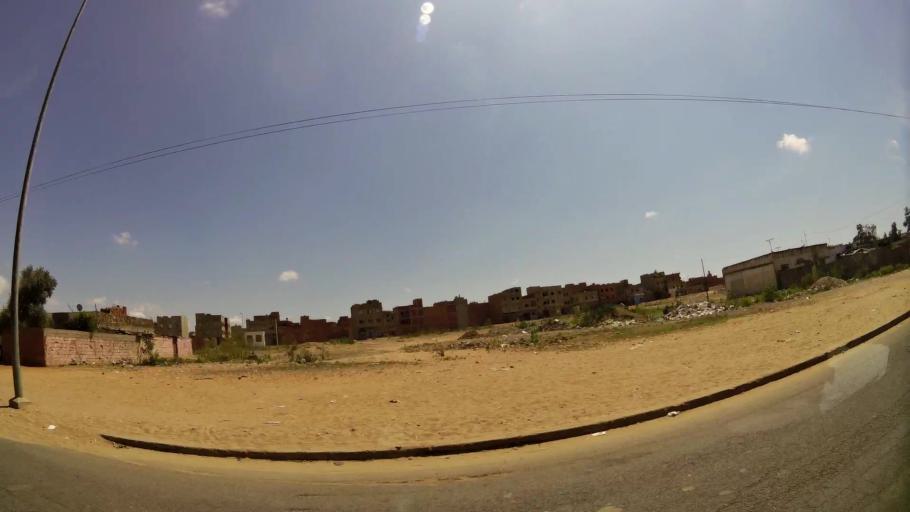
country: MA
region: Gharb-Chrarda-Beni Hssen
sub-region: Kenitra Province
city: Kenitra
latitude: 34.2305
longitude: -6.5375
